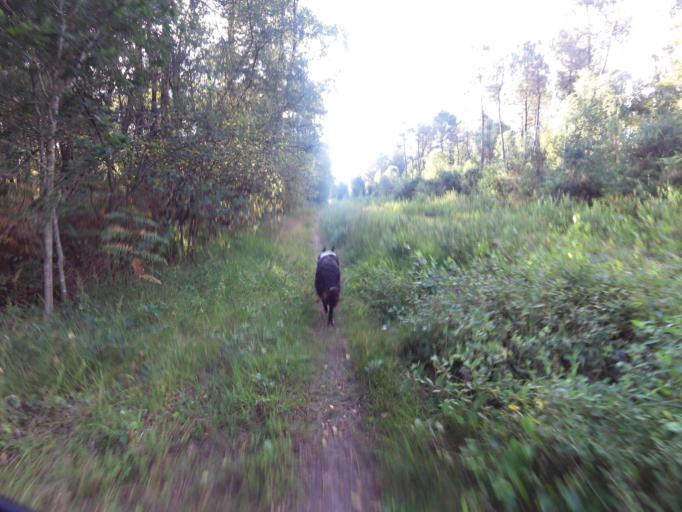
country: FR
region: Brittany
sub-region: Departement du Morbihan
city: Molac
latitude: 47.7391
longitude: -2.4249
